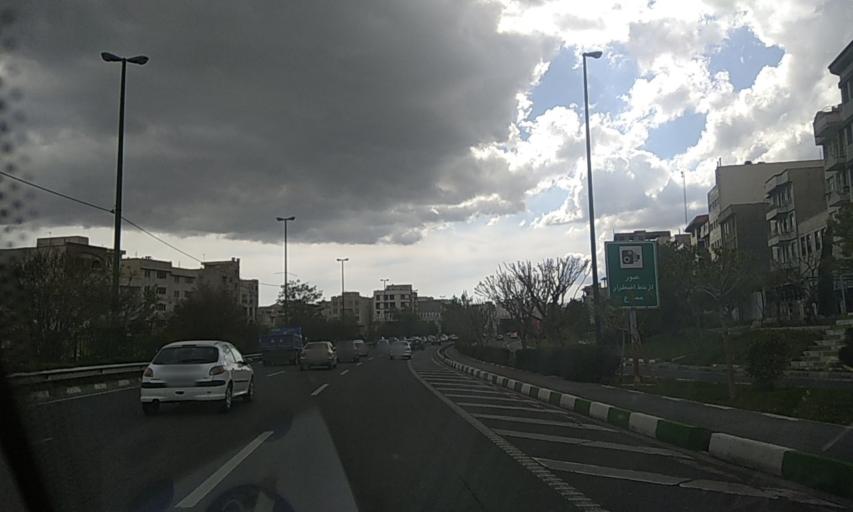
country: IR
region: Tehran
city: Tajrish
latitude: 35.7697
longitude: 51.3329
